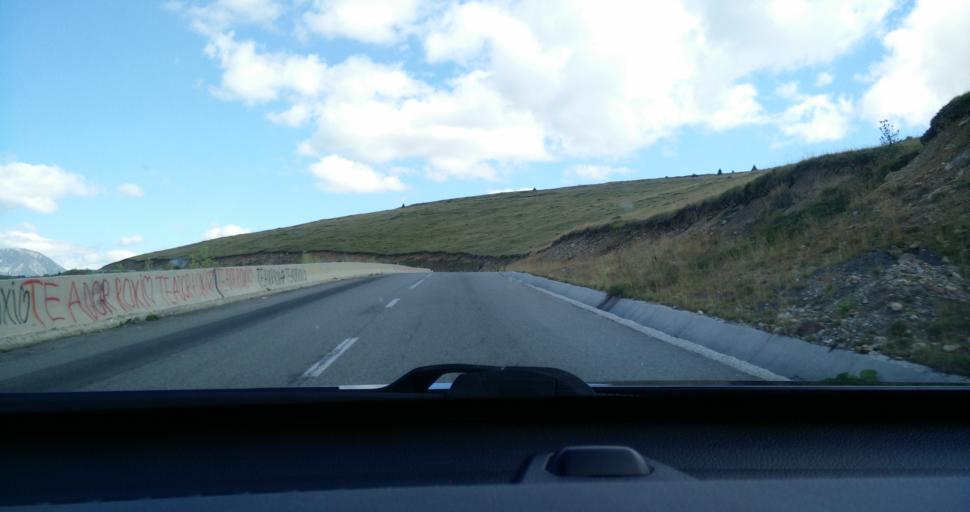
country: RO
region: Gorj
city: Novaci-Straini
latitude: 45.2549
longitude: 23.6975
